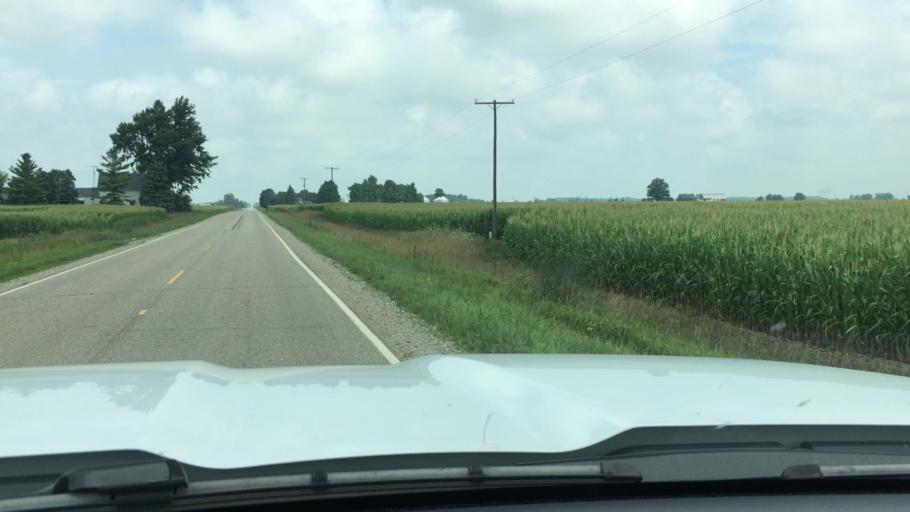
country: US
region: Michigan
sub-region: Sanilac County
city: Marlette
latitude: 43.3800
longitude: -83.0066
